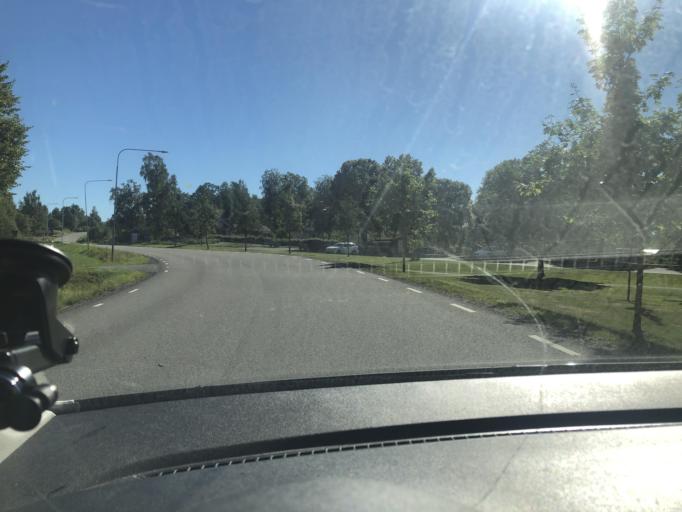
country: SE
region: Joenkoeping
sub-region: Jonkopings Kommun
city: Huskvarna
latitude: 57.7960
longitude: 14.3132
